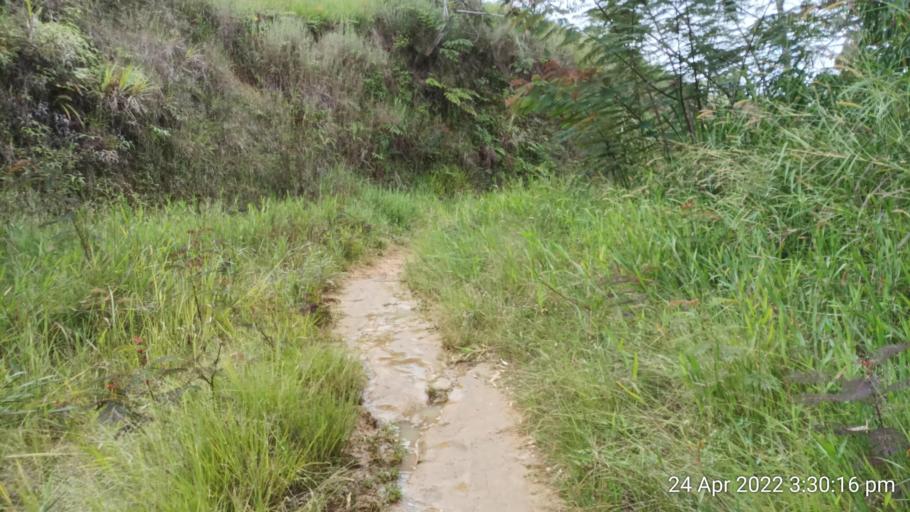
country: PG
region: Jiwaka
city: Minj
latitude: -5.8899
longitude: 144.8197
